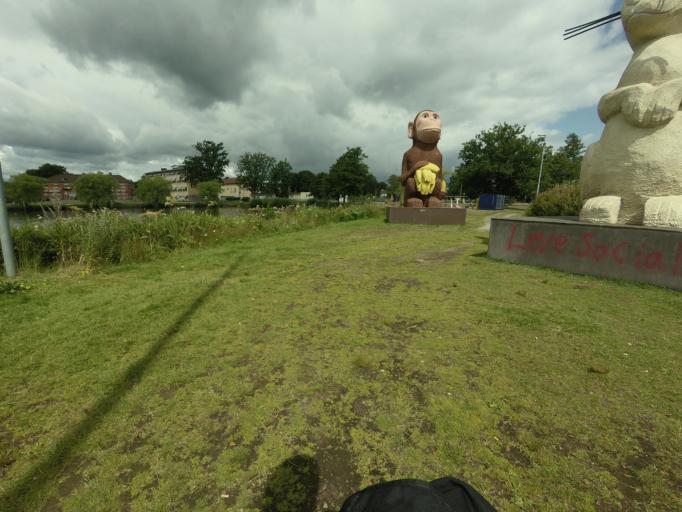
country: SE
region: Skane
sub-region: Osby Kommun
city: Osby
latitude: 56.3777
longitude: 13.9993
